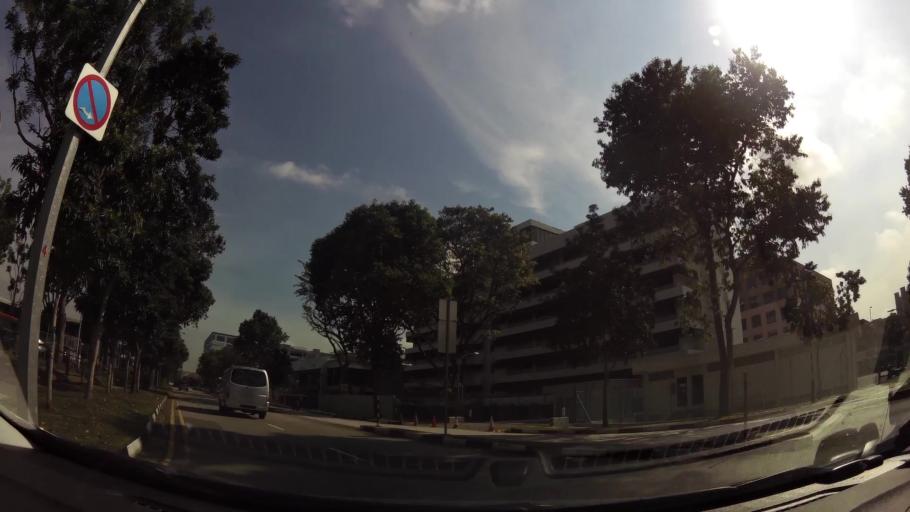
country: SG
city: Singapore
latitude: 1.3563
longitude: 103.8362
